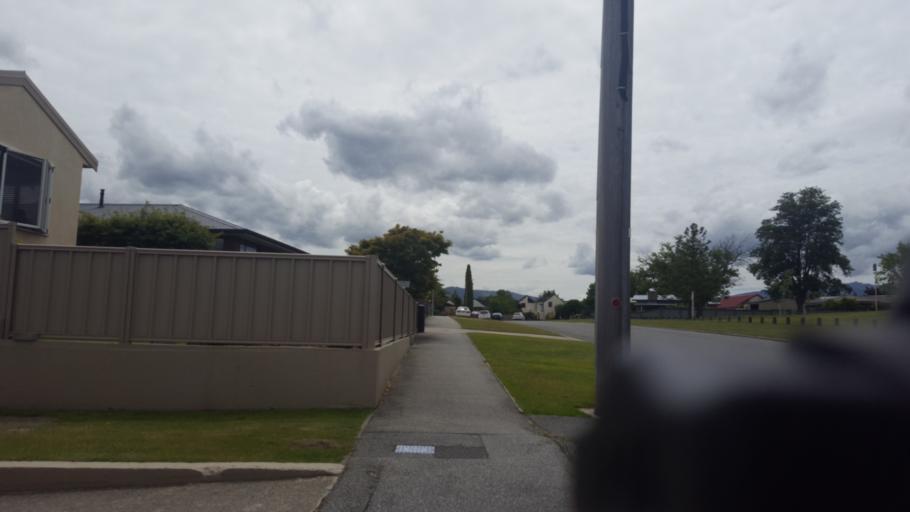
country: NZ
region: Otago
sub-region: Queenstown-Lakes District
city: Wanaka
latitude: -45.2475
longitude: 169.3792
